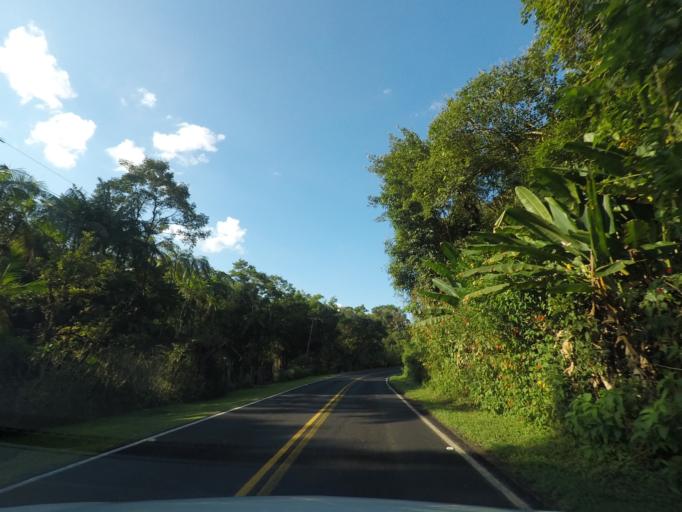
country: BR
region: Parana
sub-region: Antonina
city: Antonina
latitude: -25.3972
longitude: -48.8697
